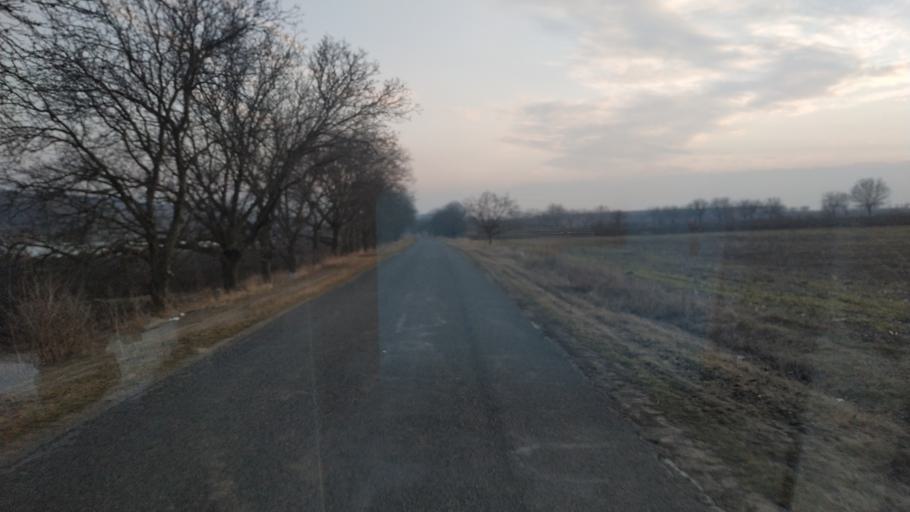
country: MD
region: Hincesti
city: Dancu
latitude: 46.6993
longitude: 28.3372
